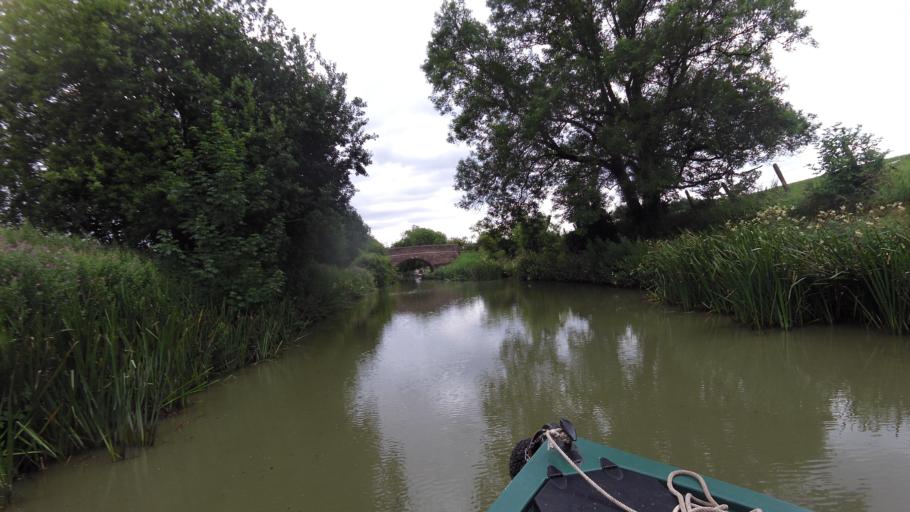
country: GB
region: England
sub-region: Wiltshire
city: Burbage
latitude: 51.3613
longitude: -1.6506
